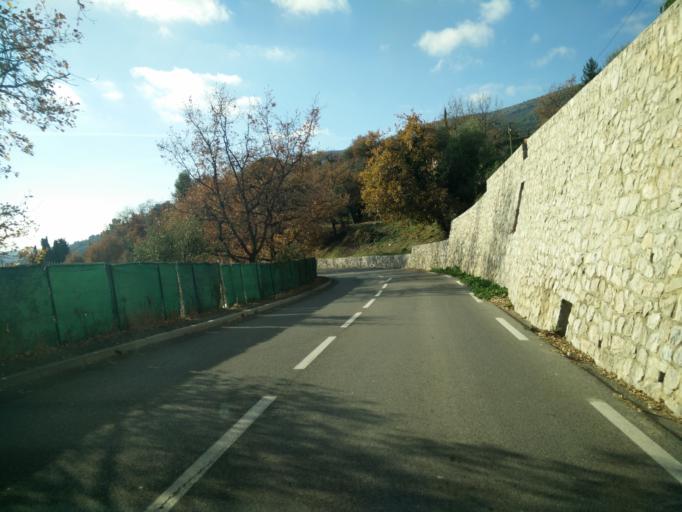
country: FR
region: Provence-Alpes-Cote d'Azur
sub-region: Departement des Alpes-Maritimes
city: Carros
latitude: 43.7881
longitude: 7.1836
